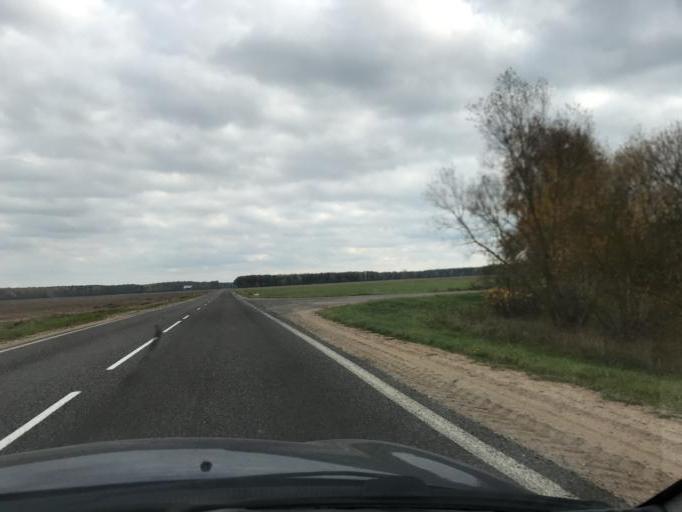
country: BY
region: Grodnenskaya
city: Lida
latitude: 53.7478
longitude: 25.2618
